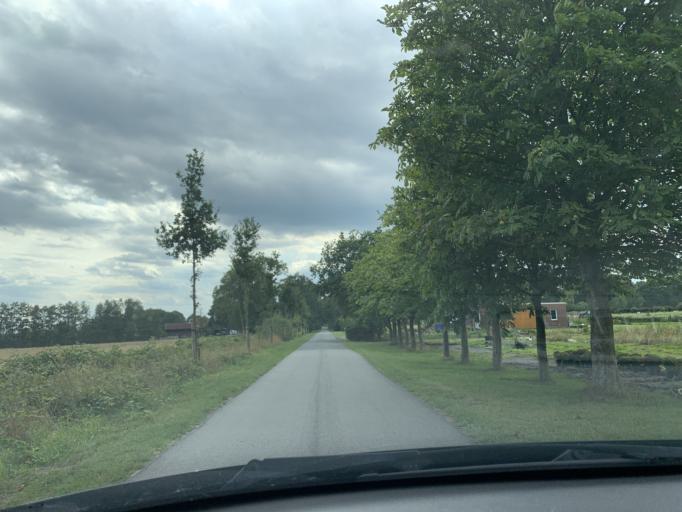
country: DE
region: Lower Saxony
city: Westerstede
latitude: 53.2522
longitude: 7.8814
